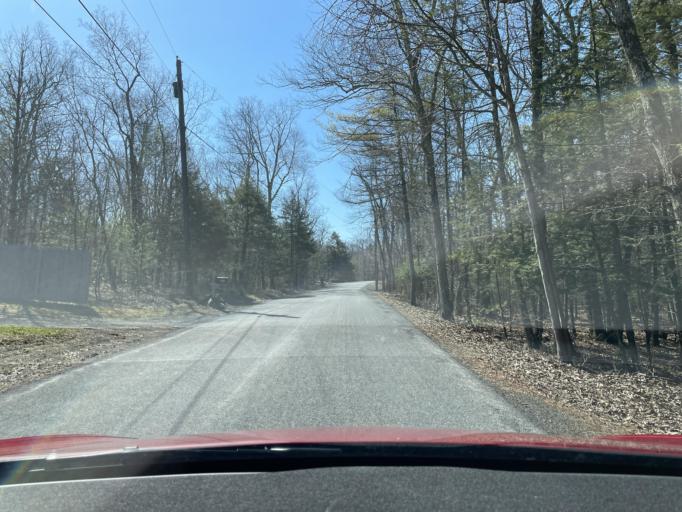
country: US
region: New York
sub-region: Ulster County
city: Zena
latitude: 42.0580
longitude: -74.0253
